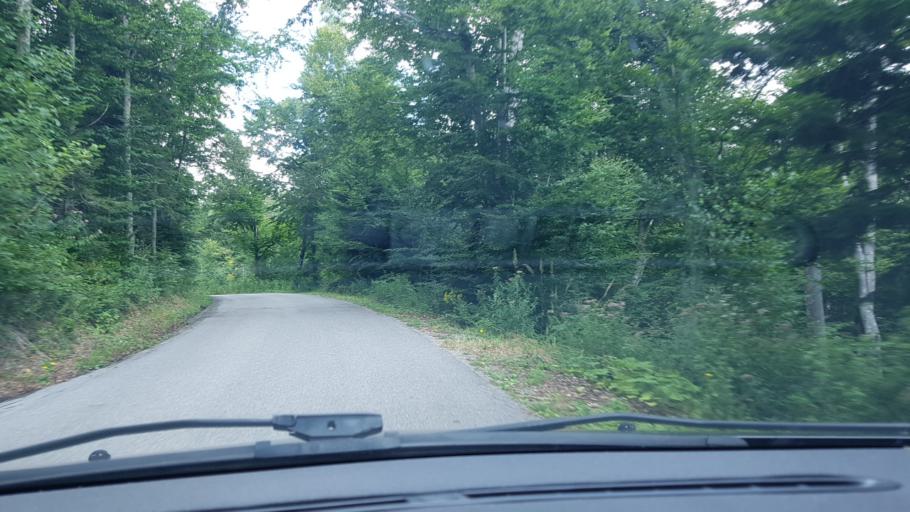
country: HR
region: Primorsko-Goranska
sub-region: Grad Delnice
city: Delnice
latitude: 45.3735
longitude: 14.7064
